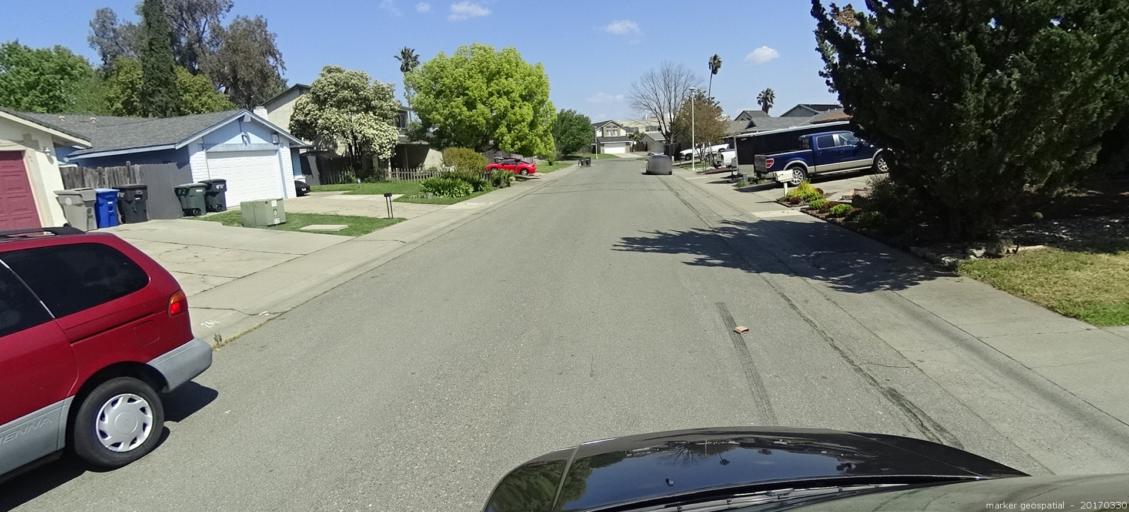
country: US
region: California
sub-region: Sacramento County
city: Florin
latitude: 38.4673
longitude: -121.4215
